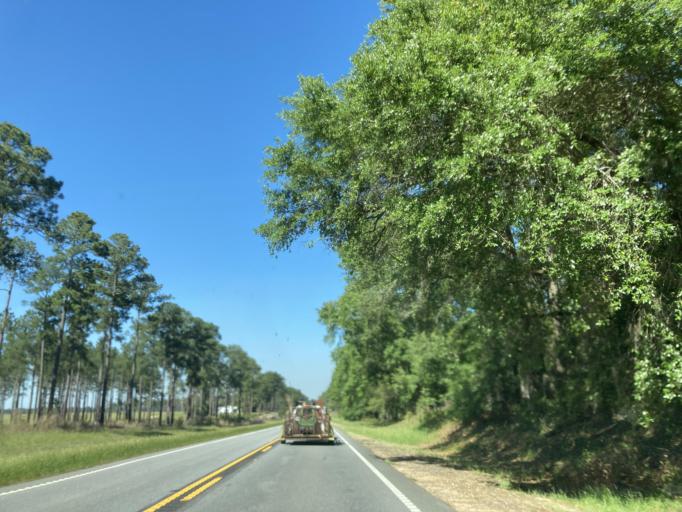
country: US
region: Georgia
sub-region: Baker County
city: Newton
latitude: 31.3600
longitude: -84.2950
